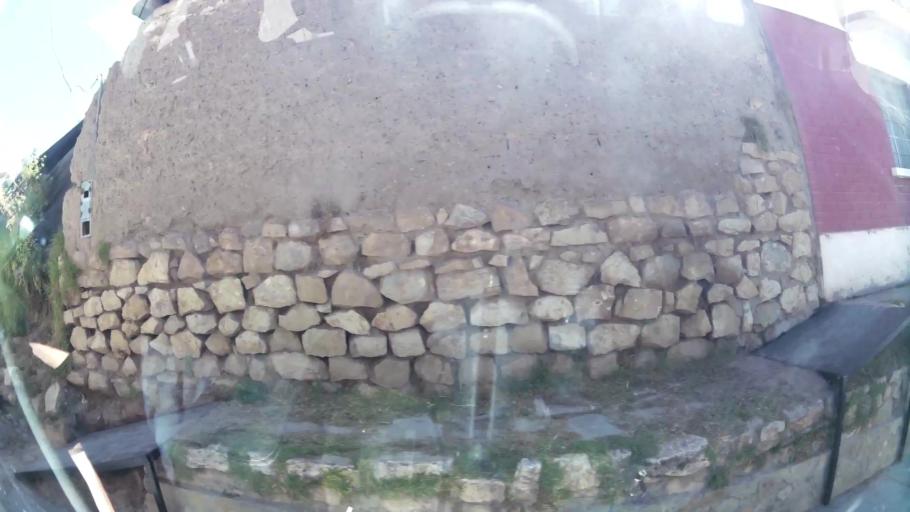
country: PE
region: Junin
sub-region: Provincia de Jauja
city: Jauja
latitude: -11.7745
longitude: -75.5037
